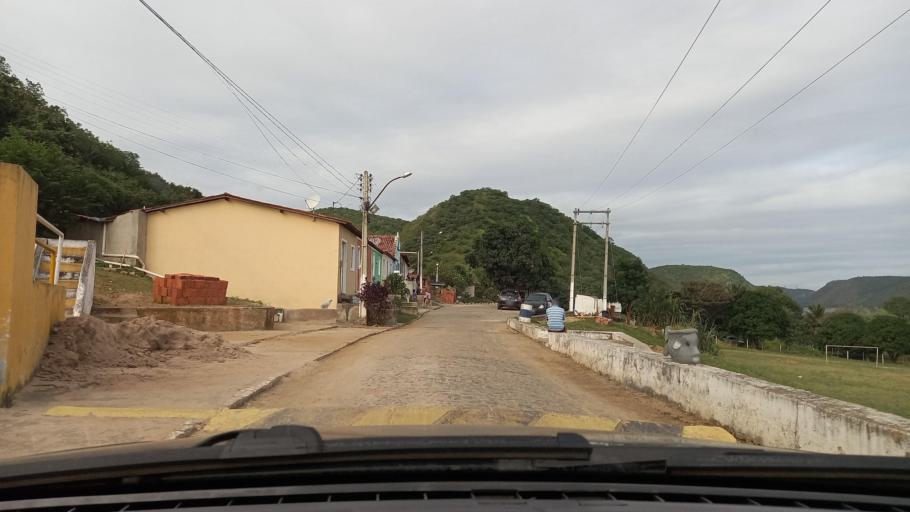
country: BR
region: Sergipe
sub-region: Caninde De Sao Francisco
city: Caninde de Sao Francisco
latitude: -9.6230
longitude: -37.7479
